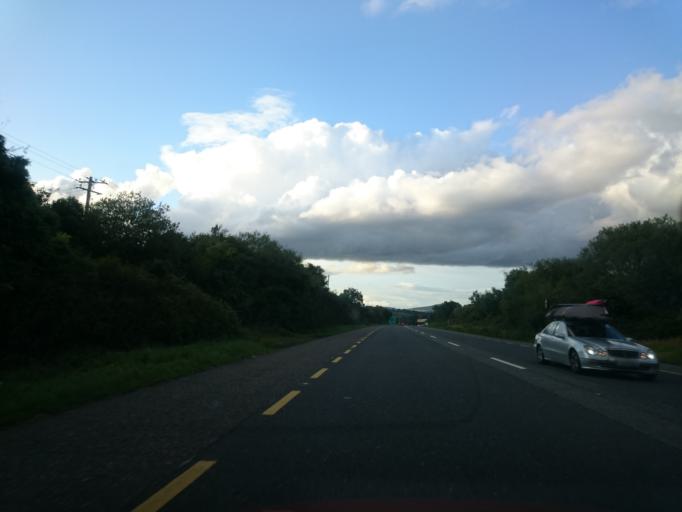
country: IE
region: Leinster
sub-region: Loch Garman
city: Enniscorthy
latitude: 52.5385
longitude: -6.5528
